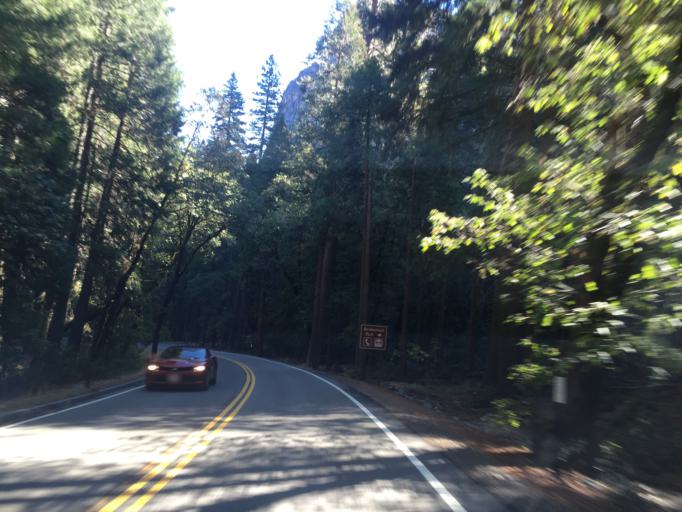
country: US
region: California
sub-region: Mariposa County
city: Yosemite Valley
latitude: 37.7164
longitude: -119.6533
